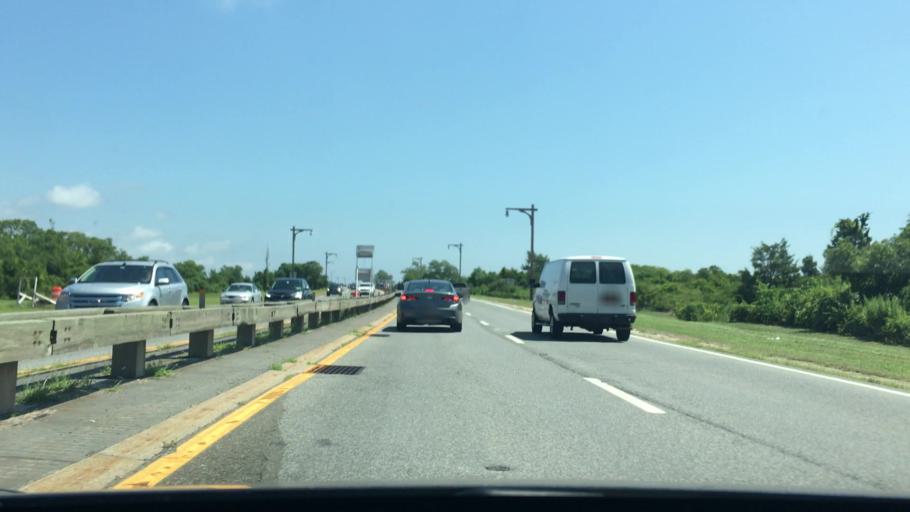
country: US
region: New York
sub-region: Nassau County
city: Point Lookout
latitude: 40.6073
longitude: -73.5579
